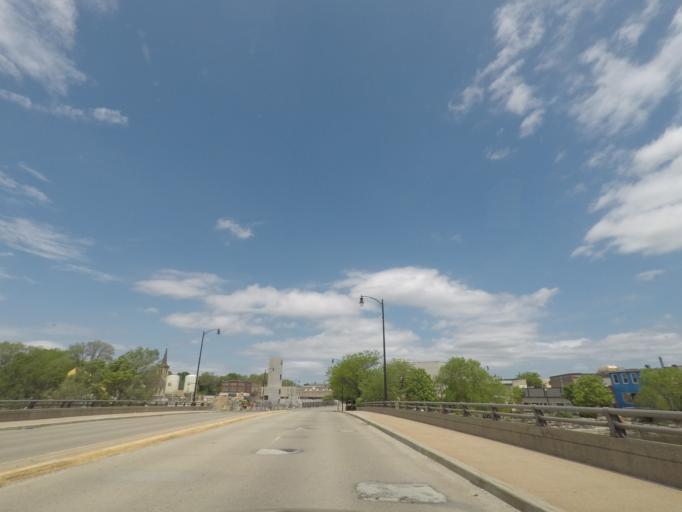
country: US
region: Illinois
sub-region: Winnebago County
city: South Beloit
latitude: 42.4998
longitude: -89.0376
